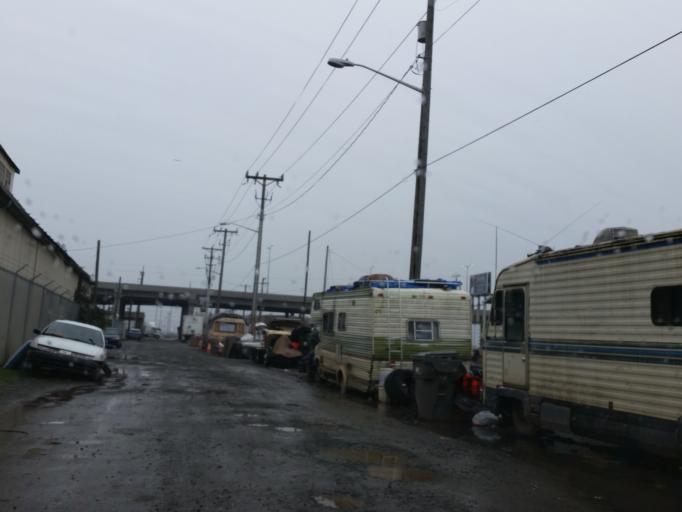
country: US
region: Washington
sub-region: King County
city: Seattle
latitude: 47.5729
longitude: -122.3367
